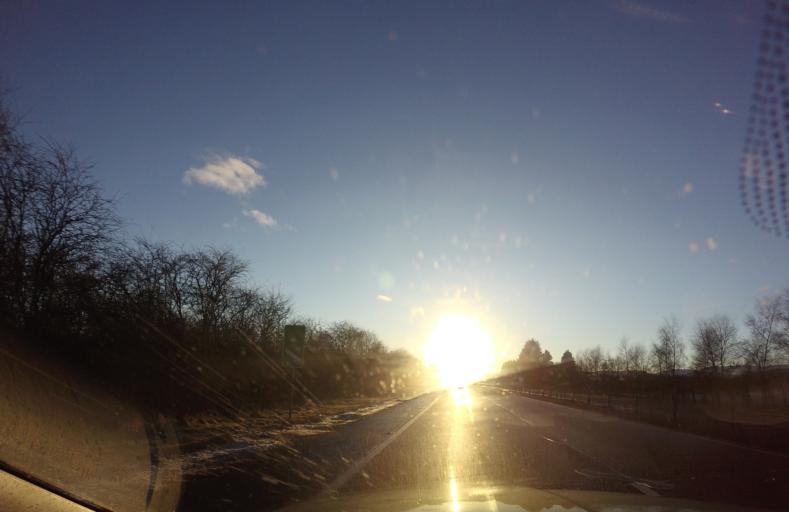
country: GB
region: Scotland
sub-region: Perth and Kinross
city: Errol
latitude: 56.4227
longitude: -3.2243
